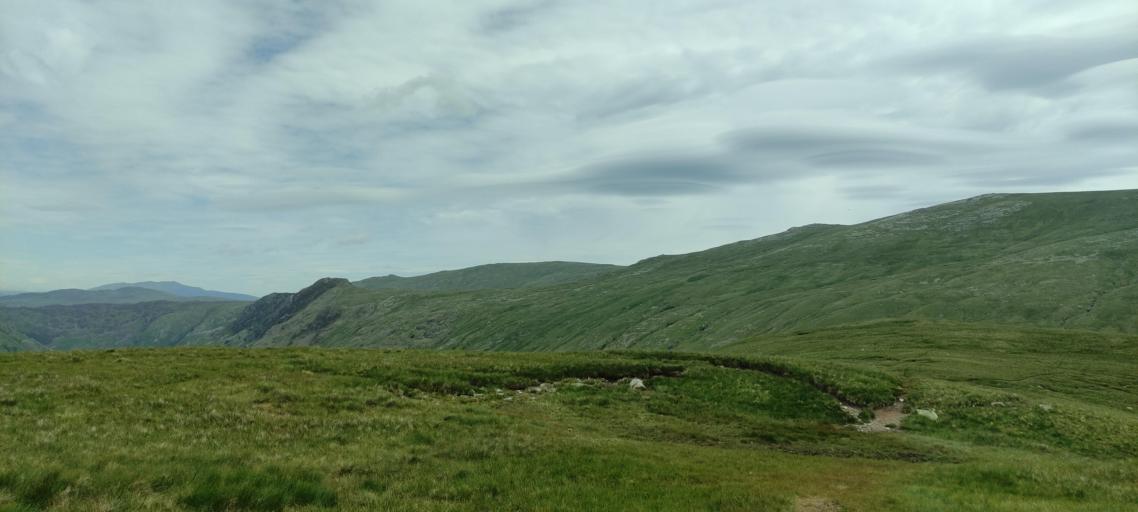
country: GB
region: England
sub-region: Cumbria
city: Keswick
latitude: 54.4692
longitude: -3.1425
